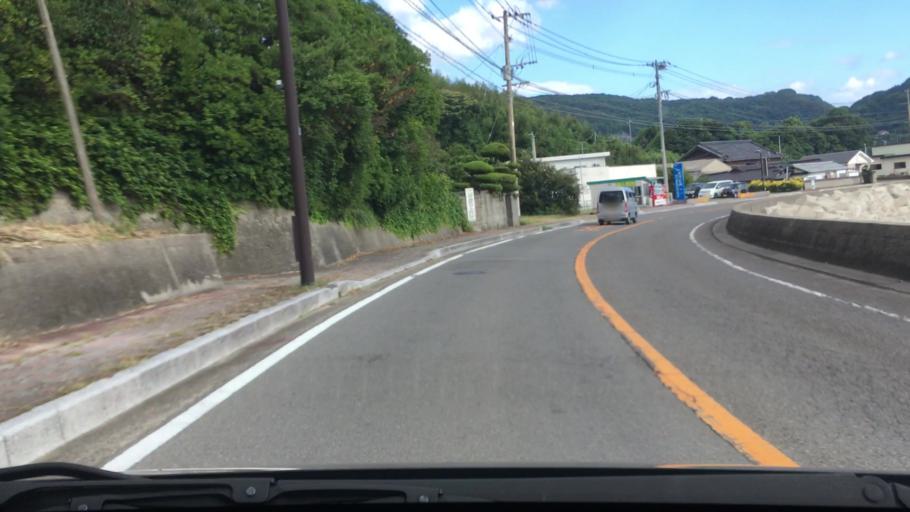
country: JP
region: Nagasaki
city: Togitsu
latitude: 32.8340
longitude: 129.7183
